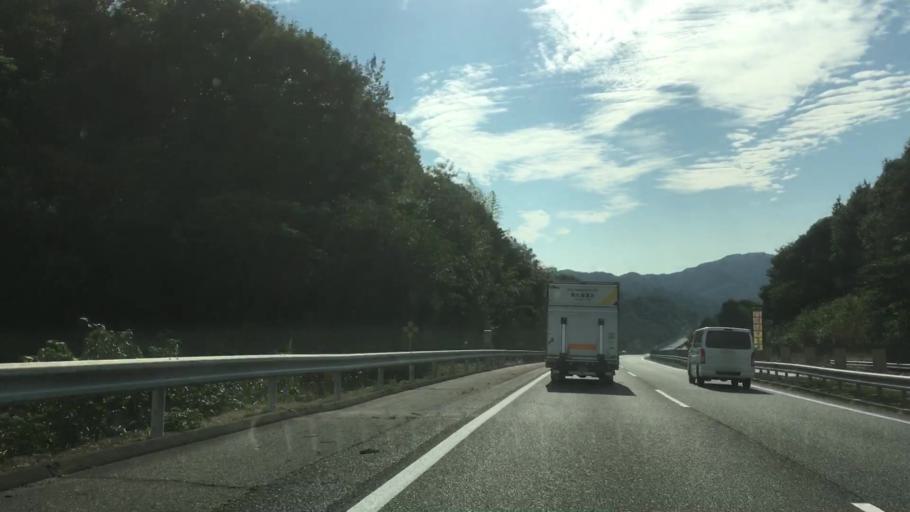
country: JP
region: Yamaguchi
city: Yanai
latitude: 34.0694
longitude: 132.0624
